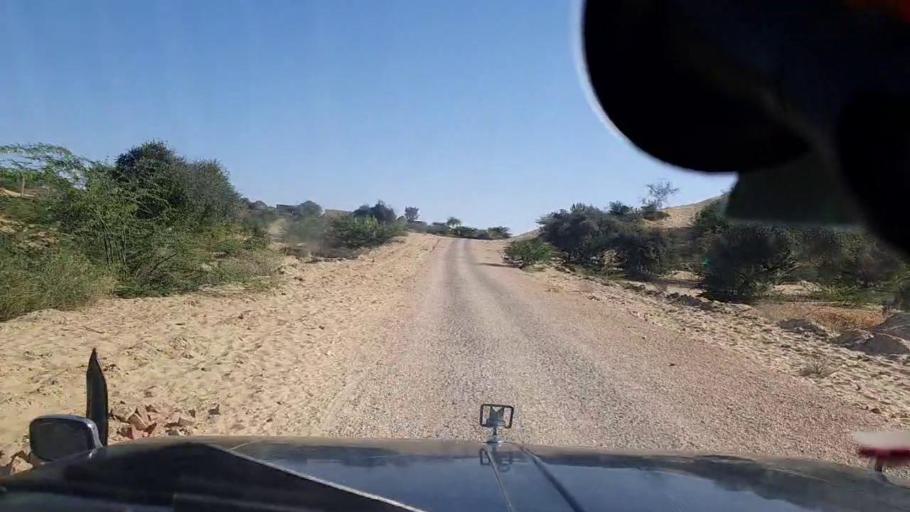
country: PK
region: Sindh
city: Diplo
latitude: 24.4727
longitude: 69.7936
